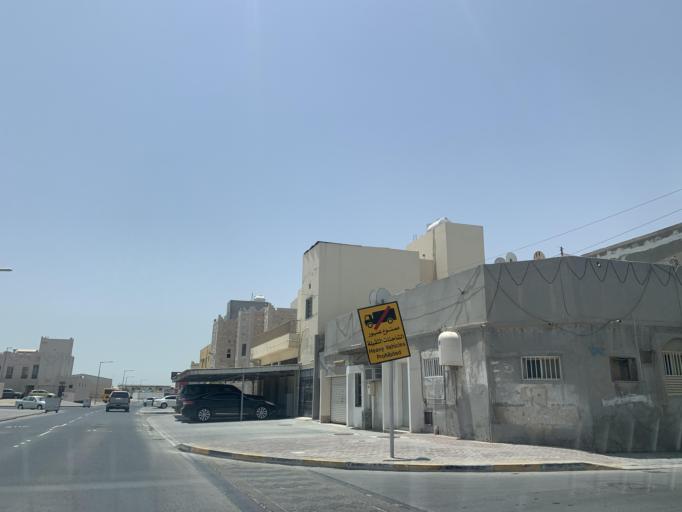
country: BH
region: Northern
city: Sitrah
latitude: 26.1589
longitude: 50.6234
